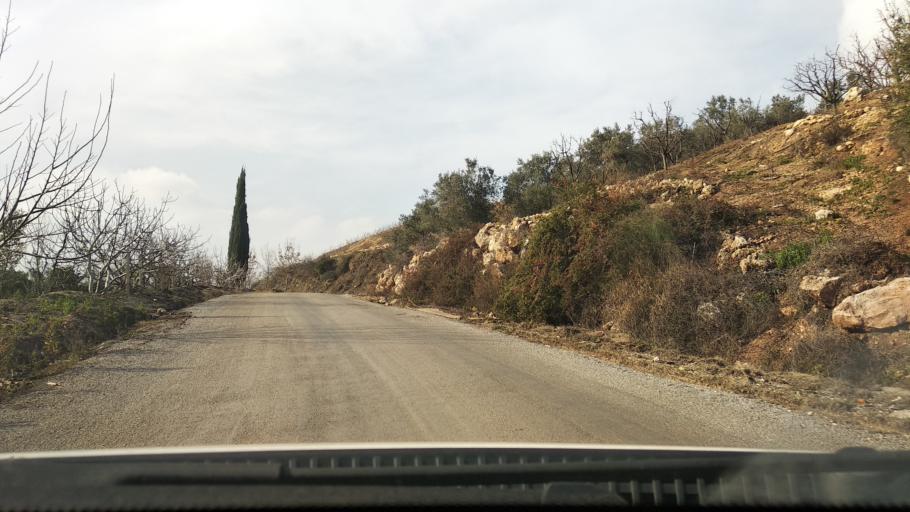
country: TR
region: Mersin
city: Kuzucubelen
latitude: 36.8689
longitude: 34.4709
